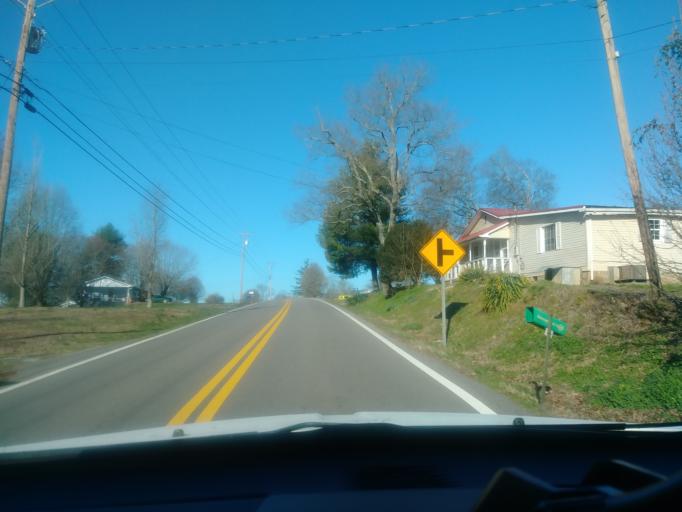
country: US
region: Tennessee
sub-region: Greene County
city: Mosheim
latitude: 36.1155
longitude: -82.9570
